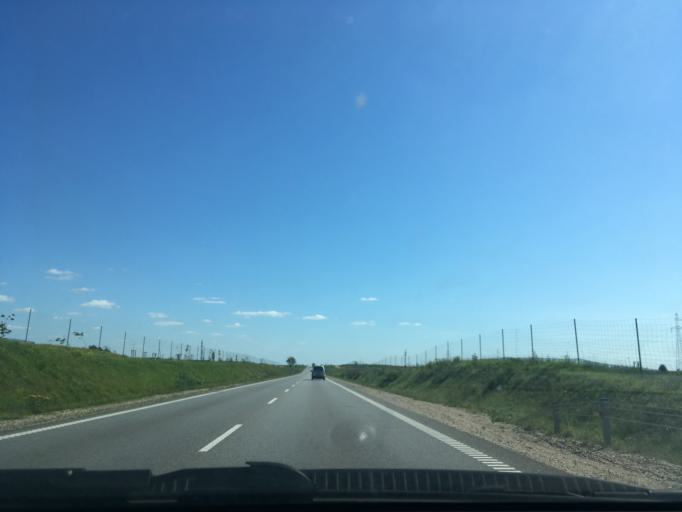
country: PL
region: Podlasie
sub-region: Powiat suwalski
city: Raczki
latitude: 53.9013
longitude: 22.8518
